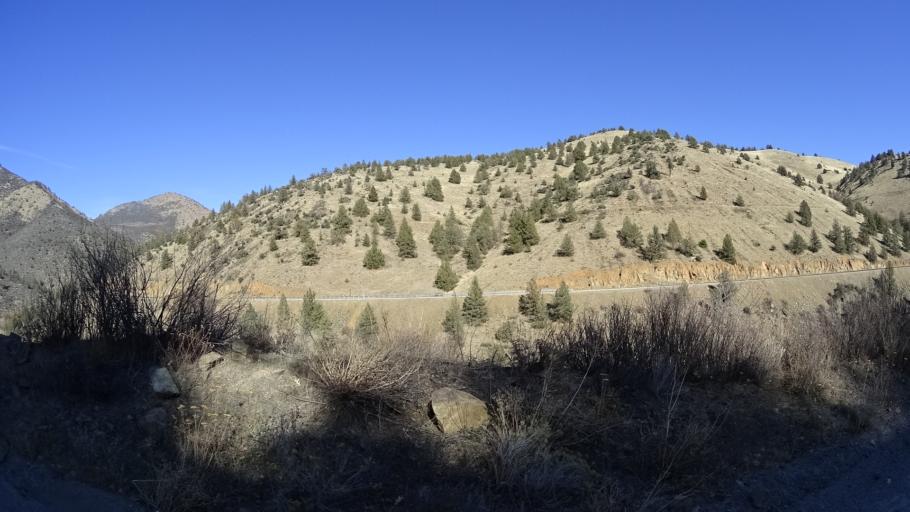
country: US
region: California
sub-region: Siskiyou County
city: Yreka
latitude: 41.7890
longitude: -122.6062
